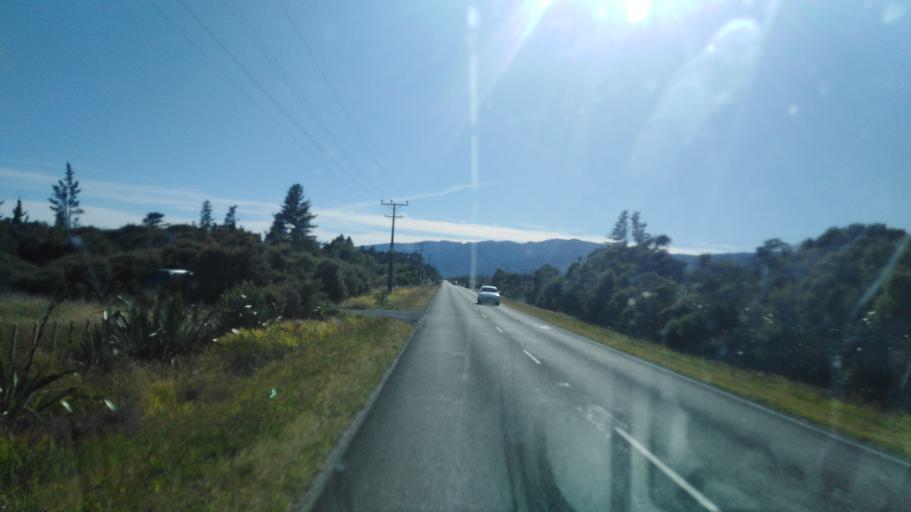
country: NZ
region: West Coast
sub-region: Buller District
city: Westport
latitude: -41.7457
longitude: 171.6845
